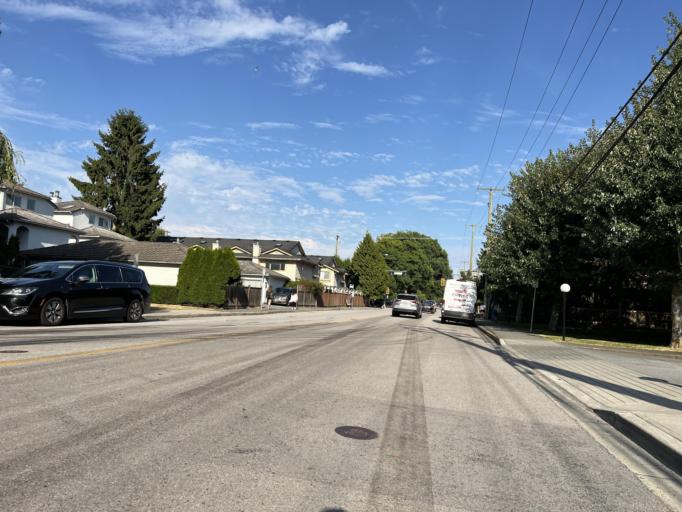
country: CA
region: British Columbia
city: Richmond
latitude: 49.1664
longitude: -123.1329
